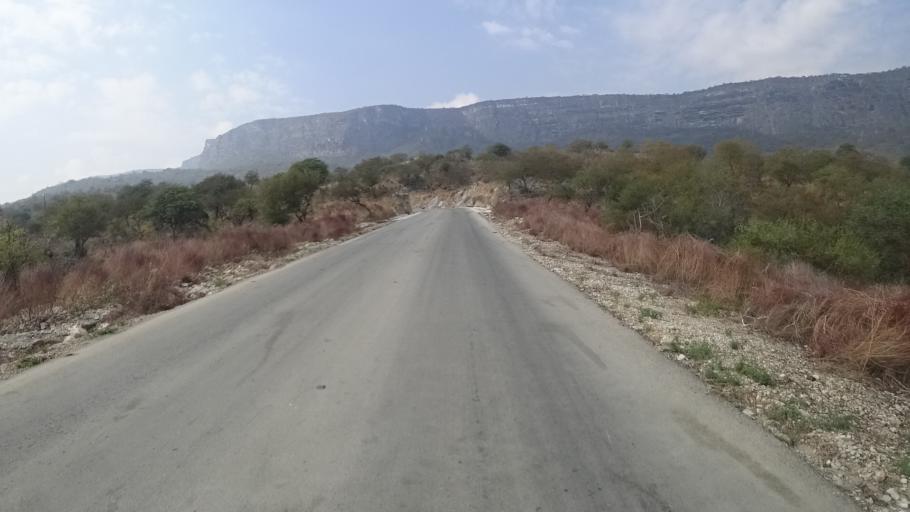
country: YE
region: Al Mahrah
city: Hawf
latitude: 16.7107
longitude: 53.2552
